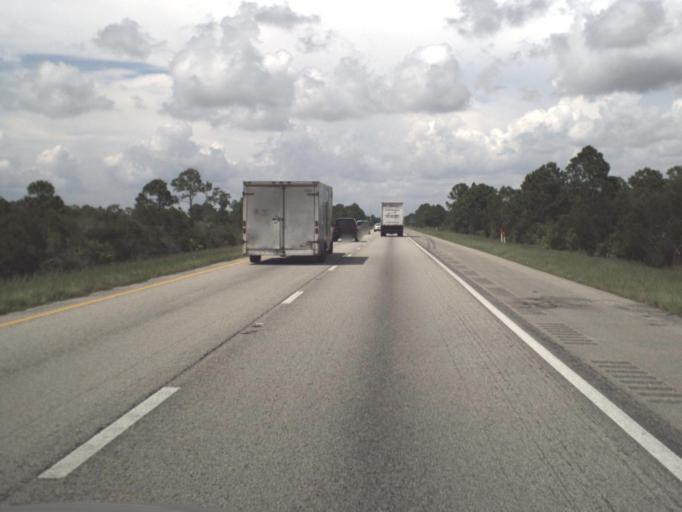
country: US
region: Florida
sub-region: Lee County
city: Burnt Store Marina
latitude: 26.8297
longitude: -81.9531
